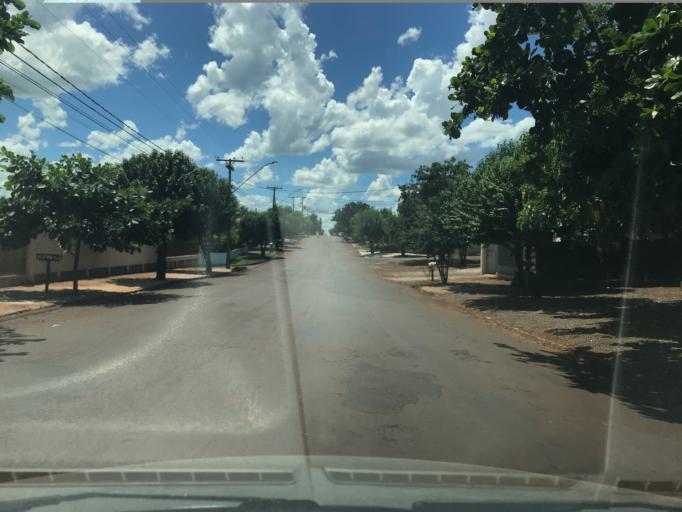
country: BR
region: Parana
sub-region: Palotina
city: Palotina
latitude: -24.2768
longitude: -53.8486
